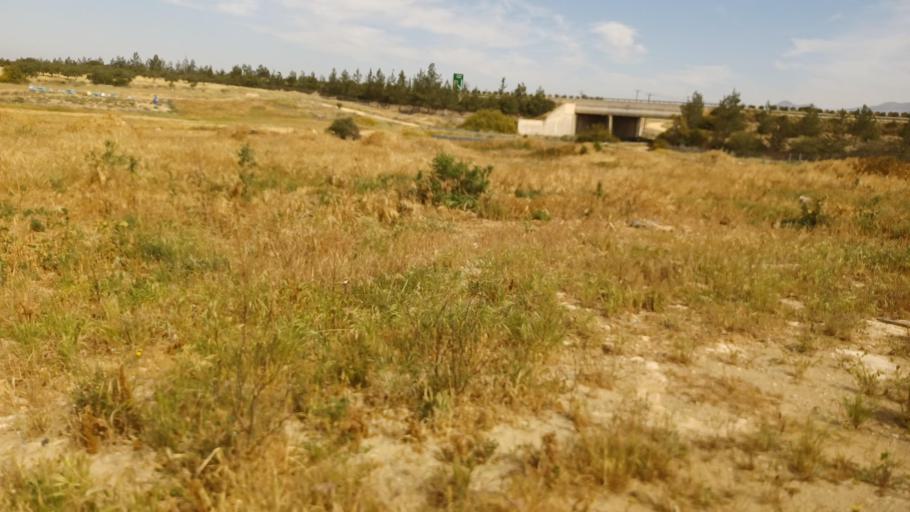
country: CY
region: Lefkosia
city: Kokkinotrimithia
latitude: 35.1599
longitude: 33.1753
